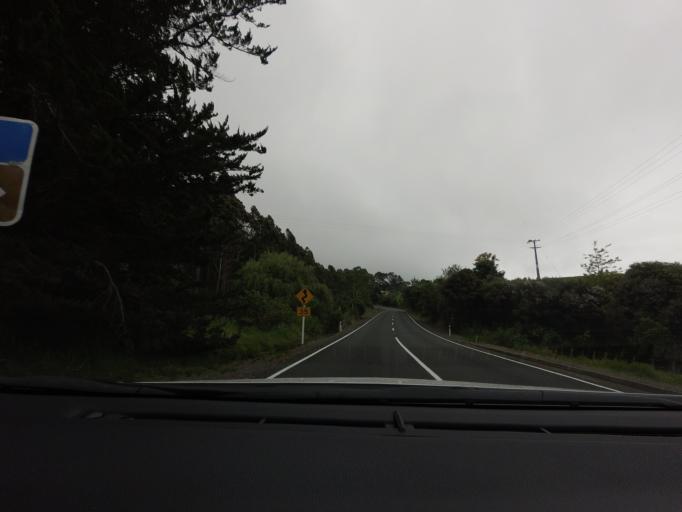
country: NZ
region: Auckland
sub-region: Auckland
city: Warkworth
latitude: -36.2829
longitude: 174.7937
